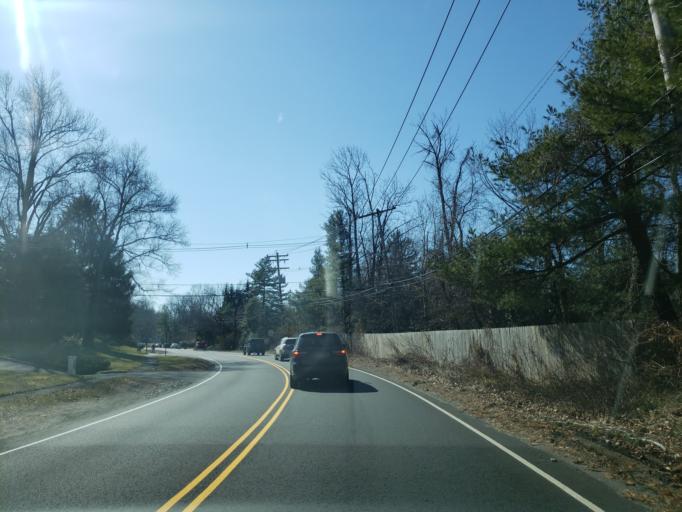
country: US
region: New Jersey
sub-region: Essex County
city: Short Hills
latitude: 40.7504
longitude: -74.3110
